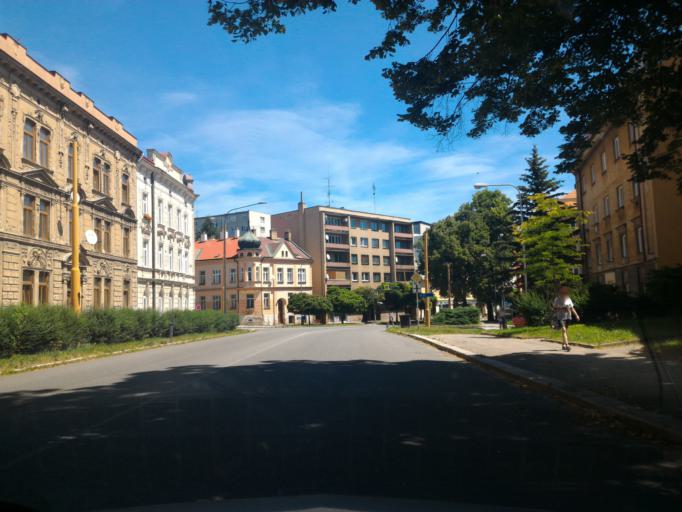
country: CZ
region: Vysocina
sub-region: Okres Jihlava
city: Jihlava
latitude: 49.3946
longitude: 15.5803
